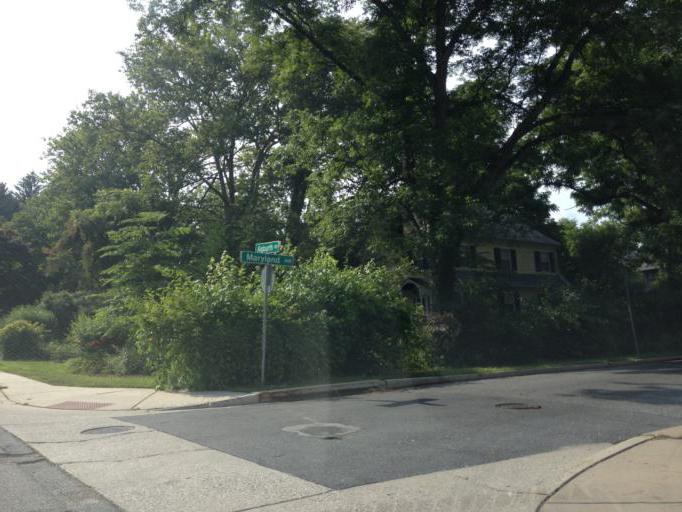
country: US
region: Maryland
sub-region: Baltimore County
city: Towson
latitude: 39.3924
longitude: -76.6004
